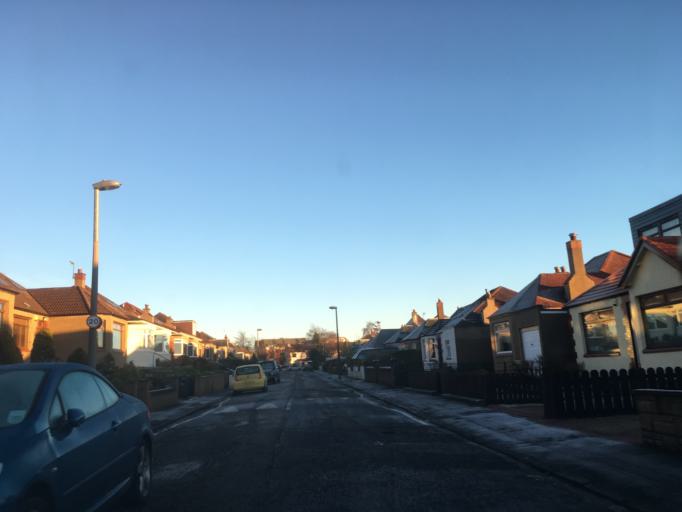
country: GB
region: Scotland
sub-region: Edinburgh
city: Currie
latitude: 55.9472
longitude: -3.2984
